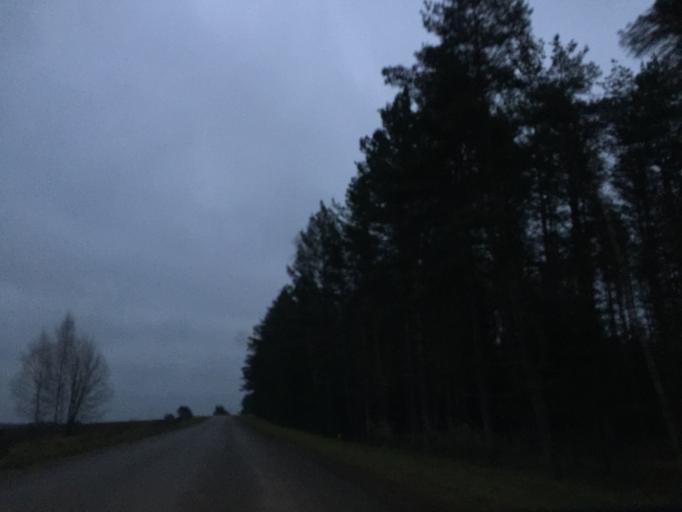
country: LV
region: Koceni
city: Koceni
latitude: 57.5512
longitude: 25.2389
